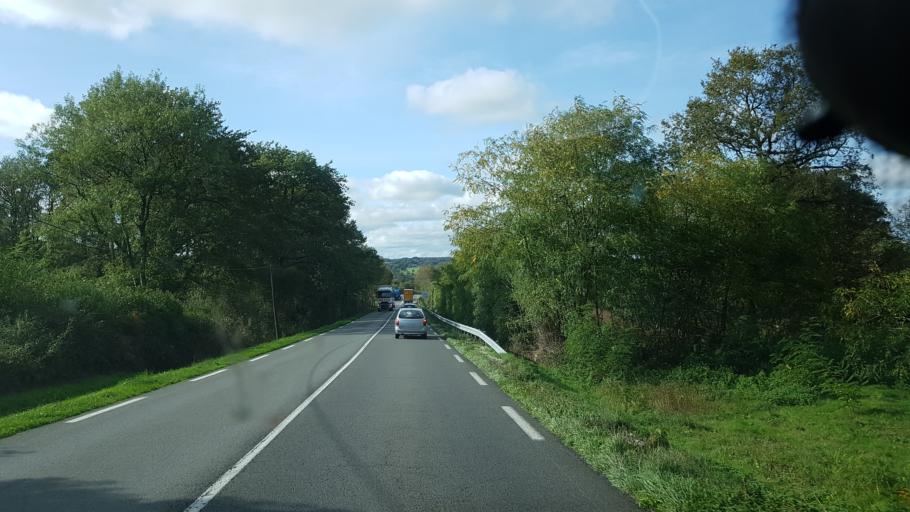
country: FR
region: Poitou-Charentes
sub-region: Departement de la Charente
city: Confolens
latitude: 46.0621
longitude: 0.6980
